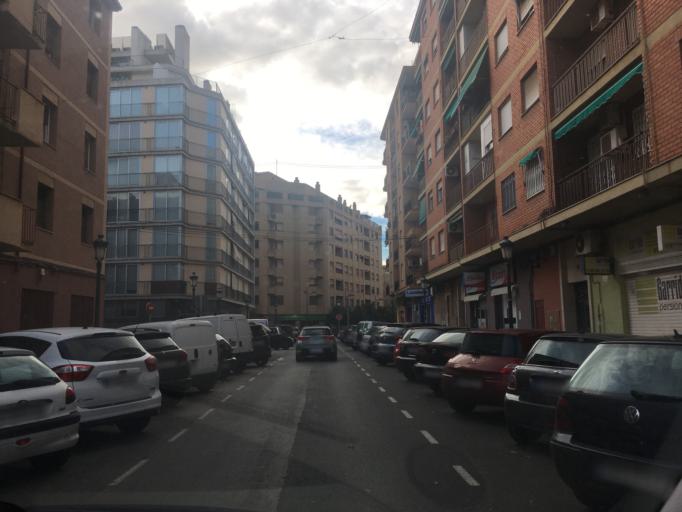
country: ES
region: Valencia
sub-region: Provincia de Valencia
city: Mislata
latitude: 39.4707
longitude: -0.4026
